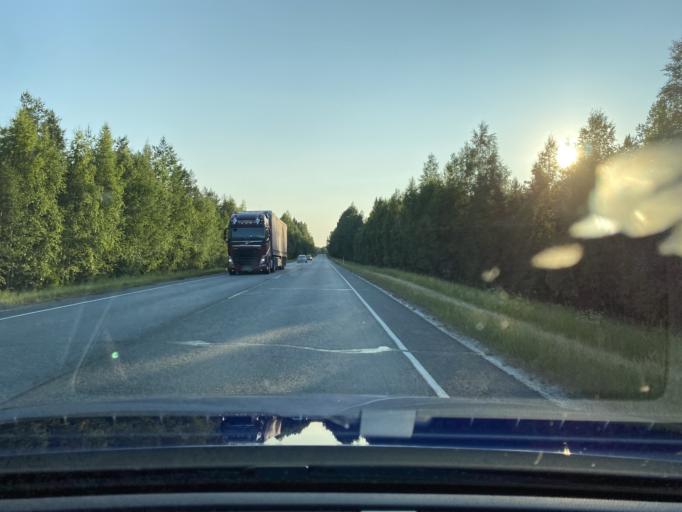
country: FI
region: Haeme
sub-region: Forssa
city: Tammela
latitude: 60.8263
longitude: 23.9448
